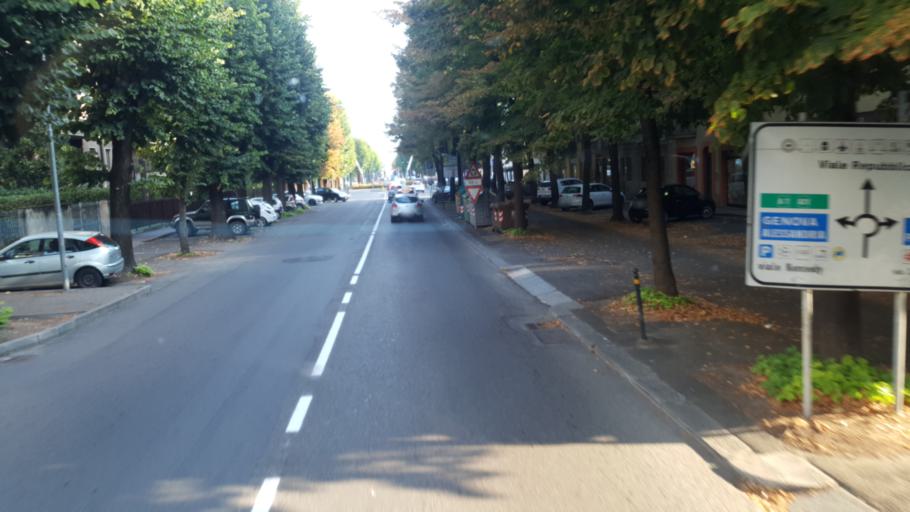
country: IT
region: Lombardy
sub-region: Provincia di Pavia
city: Voghera
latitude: 44.9850
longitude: 9.0086
